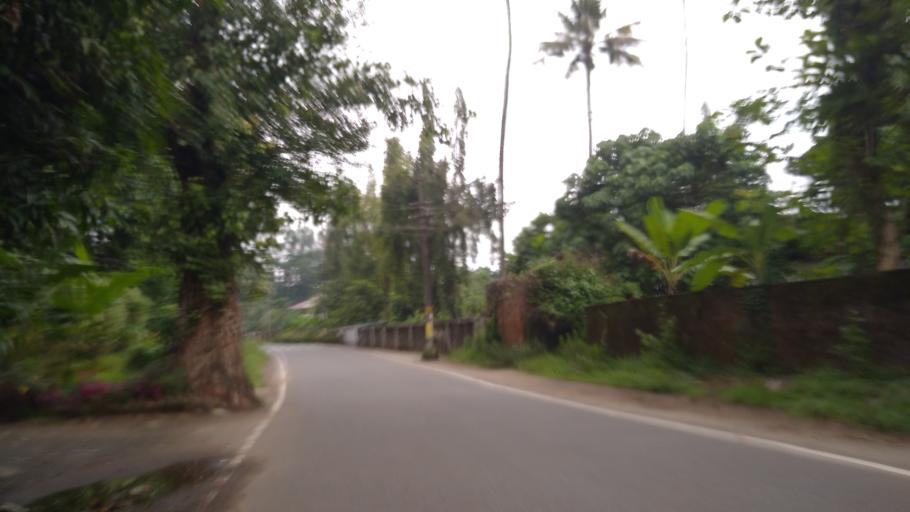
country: IN
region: Kerala
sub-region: Ernakulam
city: Perumpavur
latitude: 10.1206
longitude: 76.5343
